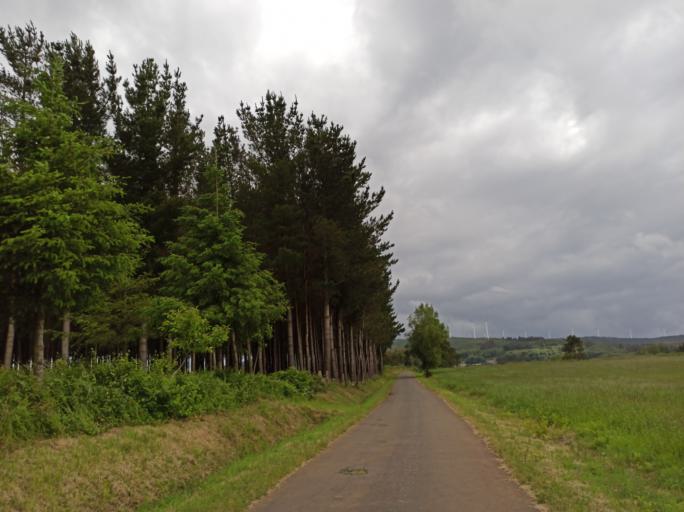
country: ES
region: Galicia
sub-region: Provincia de Pontevedra
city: Silleda
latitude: 42.7637
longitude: -8.1602
